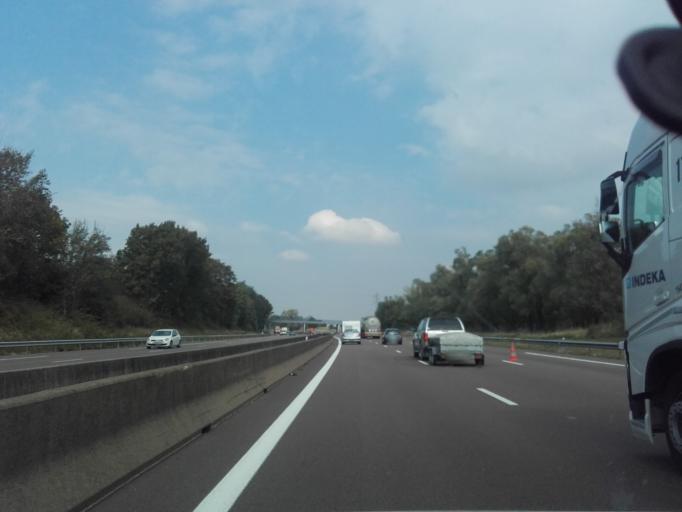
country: FR
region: Bourgogne
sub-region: Departement de Saone-et-Loire
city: Tournus
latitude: 46.5256
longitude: 4.9182
